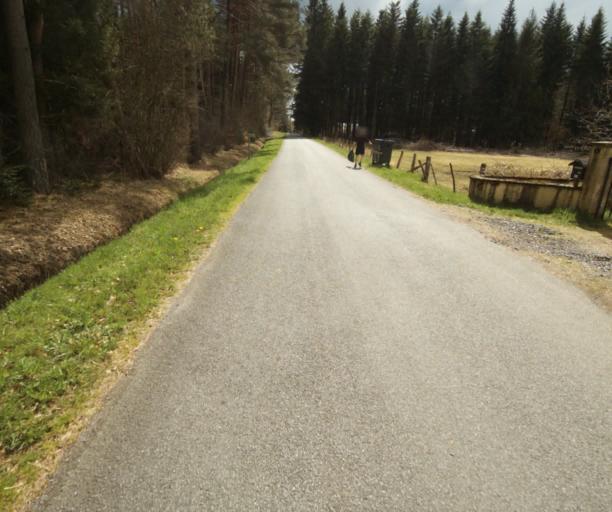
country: FR
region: Limousin
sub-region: Departement de la Correze
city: Correze
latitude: 45.2717
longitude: 1.9795
